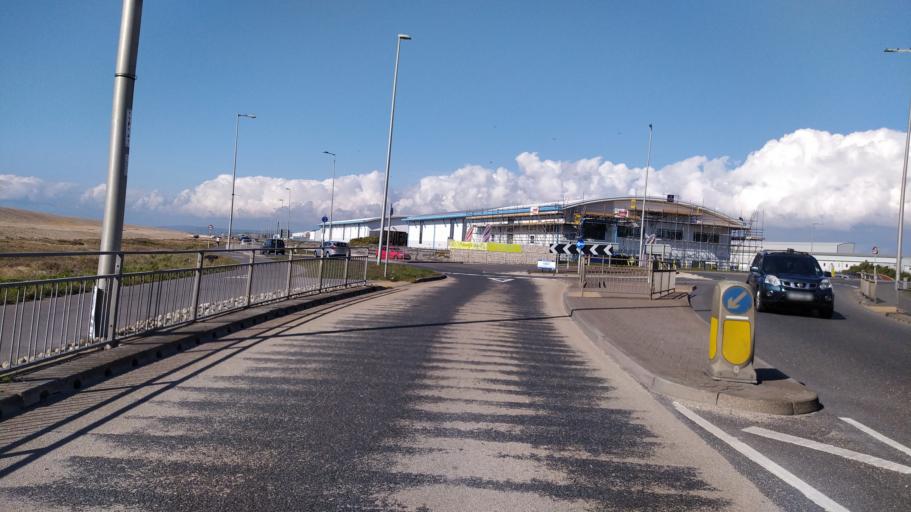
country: GB
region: England
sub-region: Dorset
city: Portland
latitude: 50.5656
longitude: -2.4530
